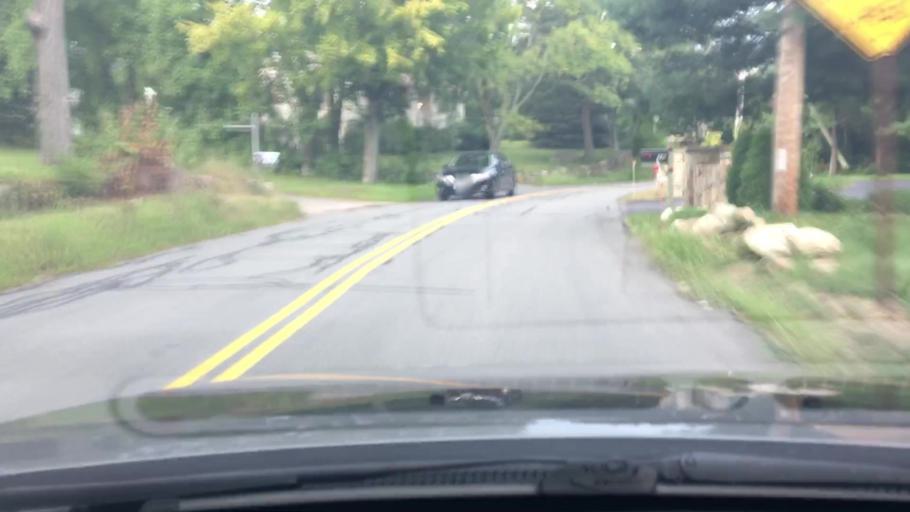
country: US
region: Massachusetts
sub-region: Worcester County
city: Milford
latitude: 42.1698
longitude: -71.5311
